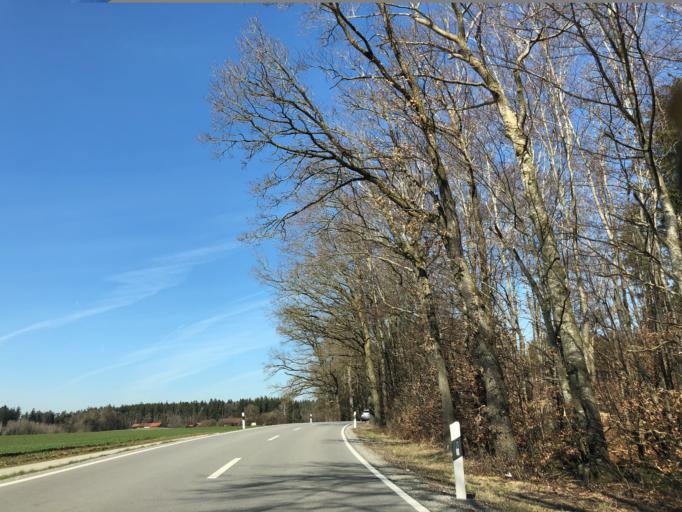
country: DE
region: Bavaria
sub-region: Upper Bavaria
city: Pfaffing
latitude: 48.0679
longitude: 12.1088
